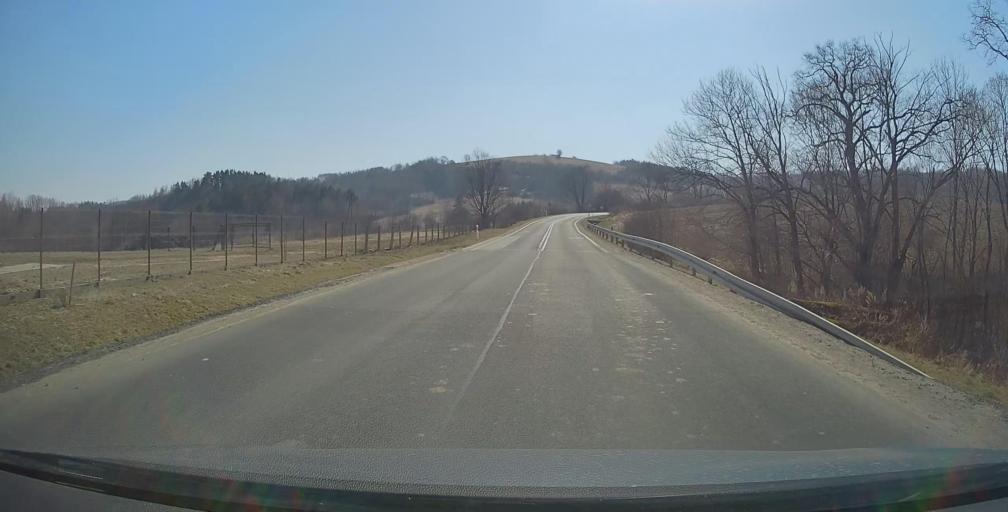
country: PL
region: Subcarpathian Voivodeship
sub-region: Powiat przemyski
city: Bircza
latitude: 49.6571
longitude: 22.4300
